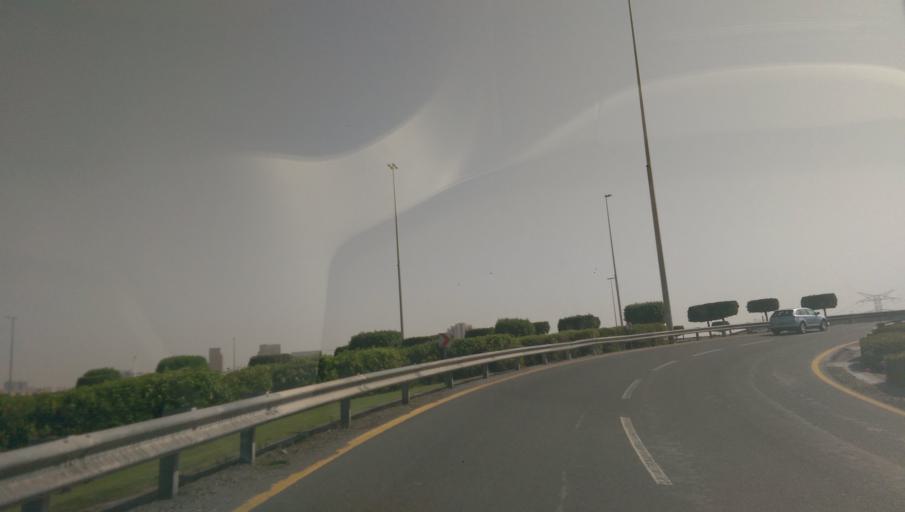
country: AE
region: Dubai
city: Dubai
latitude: 25.0768
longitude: 55.2122
